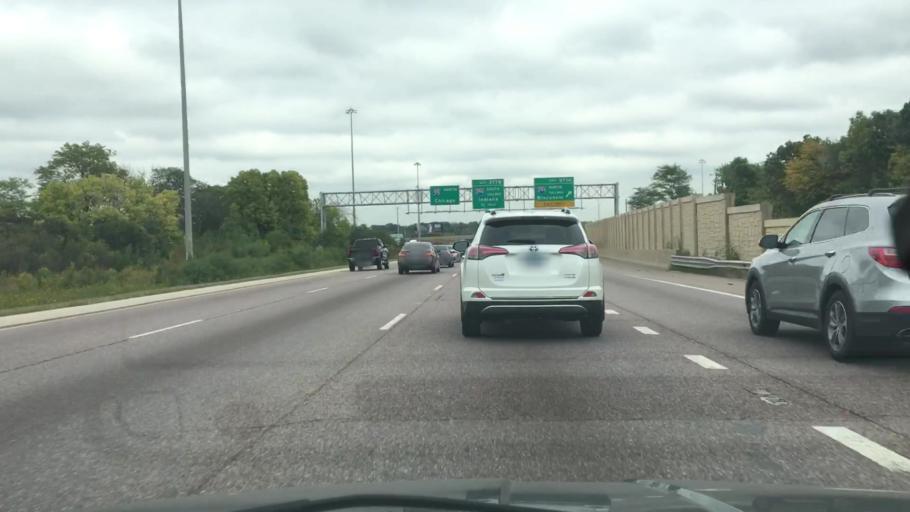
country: US
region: Illinois
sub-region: Cook County
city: Indian Head Park
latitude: 41.7593
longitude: -87.9079
